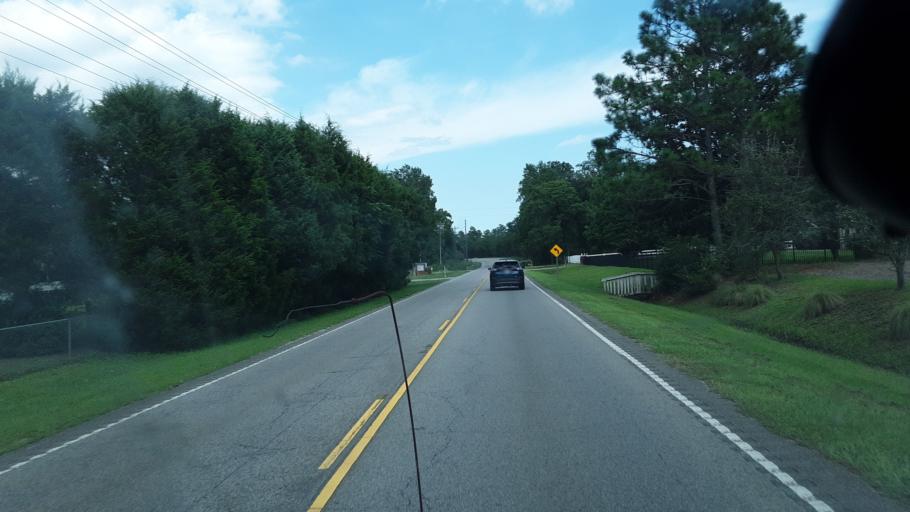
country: US
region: South Carolina
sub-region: Horry County
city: Red Hill
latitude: 33.8218
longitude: -78.9077
